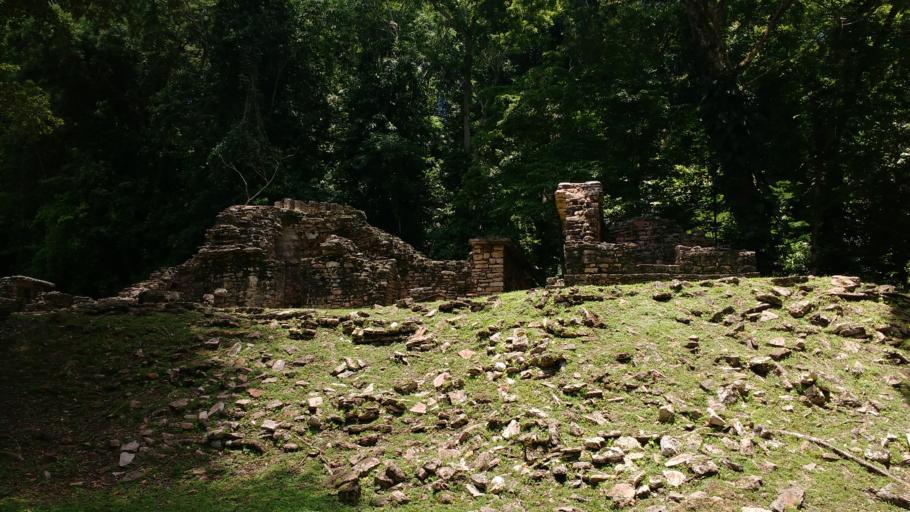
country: MX
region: Chiapas
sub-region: Ocosingo
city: Frontera Corozal
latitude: 16.8997
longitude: -90.9644
